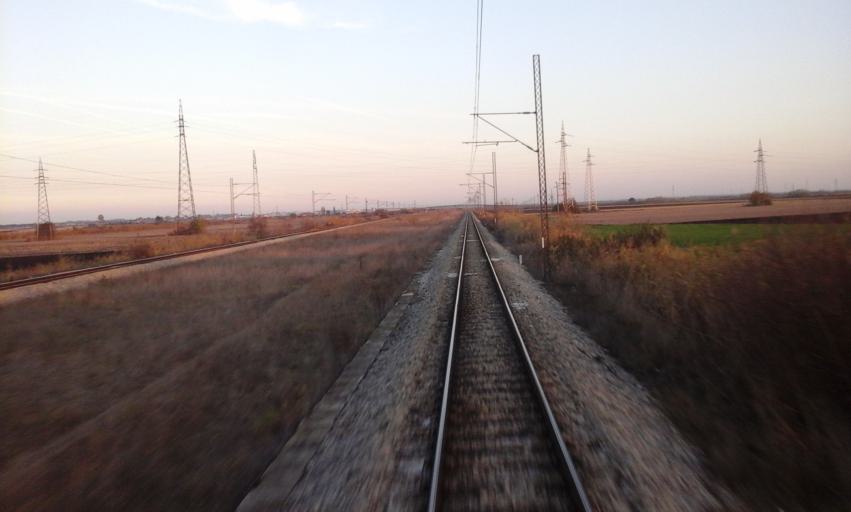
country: RS
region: Autonomna Pokrajina Vojvodina
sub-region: Sremski Okrug
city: Stara Pazova
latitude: 44.9639
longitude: 20.1641
